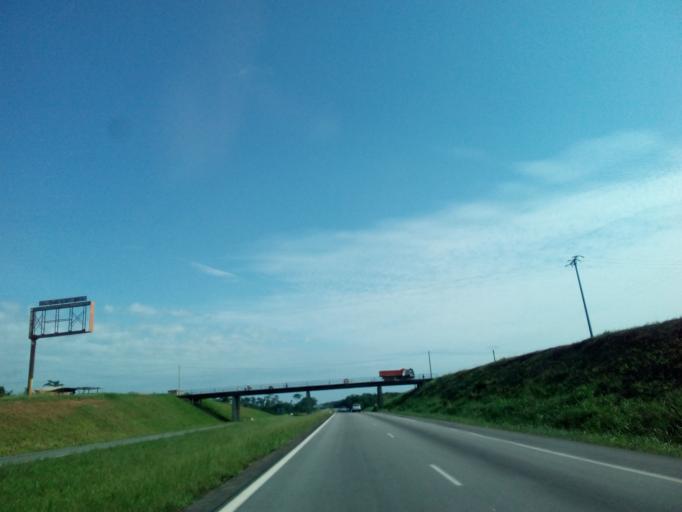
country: CI
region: Lagunes
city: Songon
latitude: 5.5218
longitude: -4.2892
